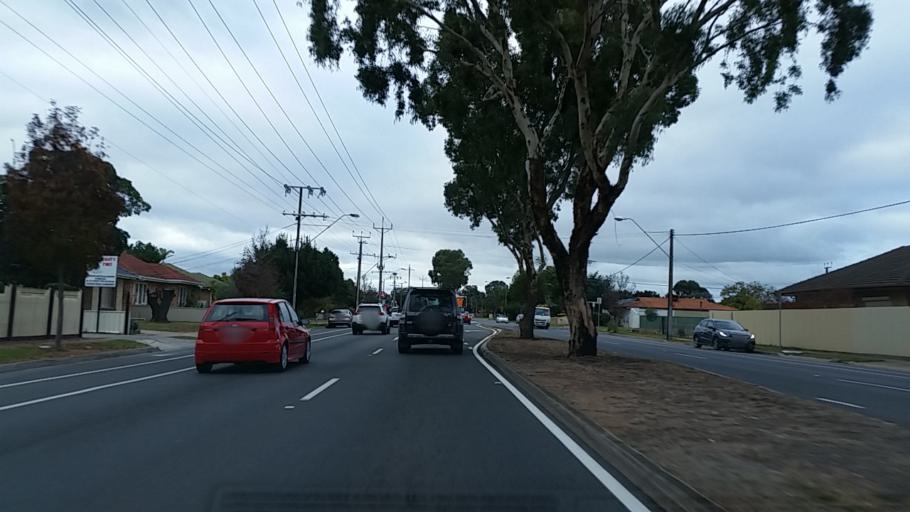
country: AU
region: South Australia
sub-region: Salisbury
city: Salisbury
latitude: -34.7731
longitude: 138.6318
